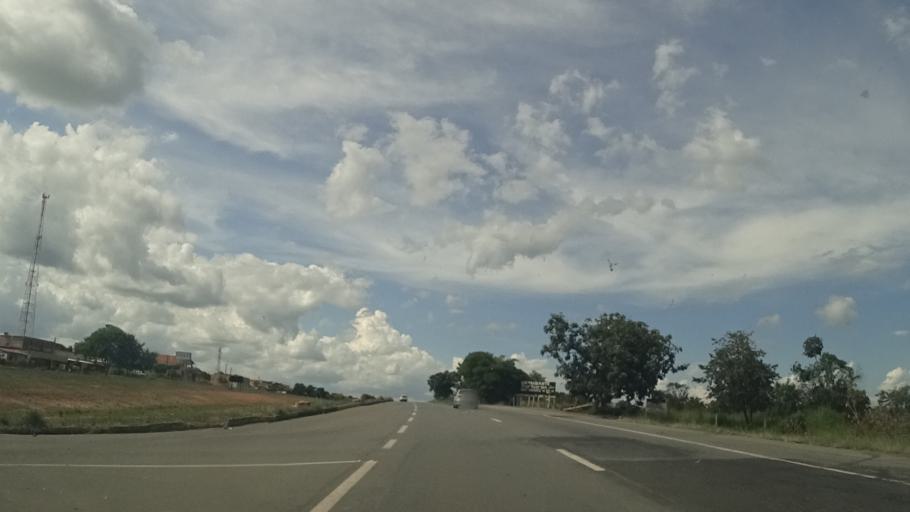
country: BR
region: Goias
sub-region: Piracanjuba
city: Piracanjuba
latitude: -17.2599
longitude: -49.2412
